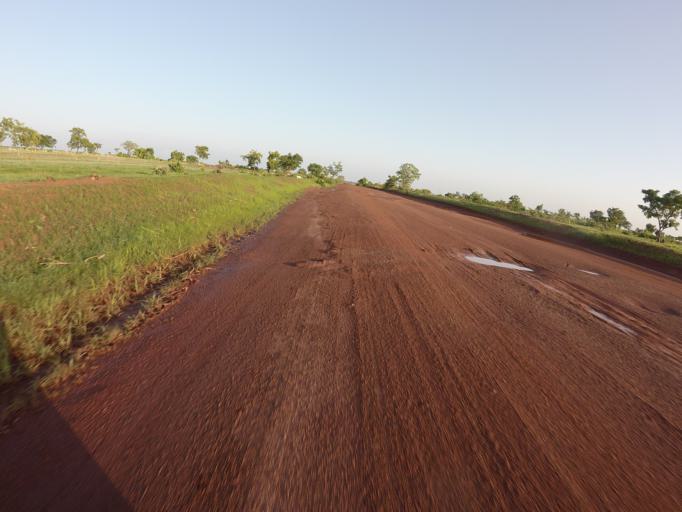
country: TG
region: Savanes
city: Sansanne-Mango
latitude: 10.2622
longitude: -0.0798
